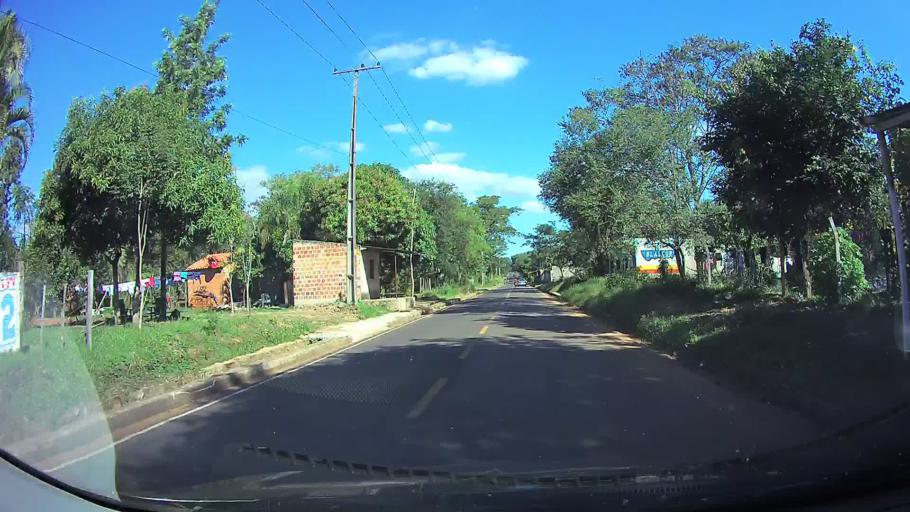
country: PY
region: Central
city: Limpio
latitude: -25.1957
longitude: -57.4771
